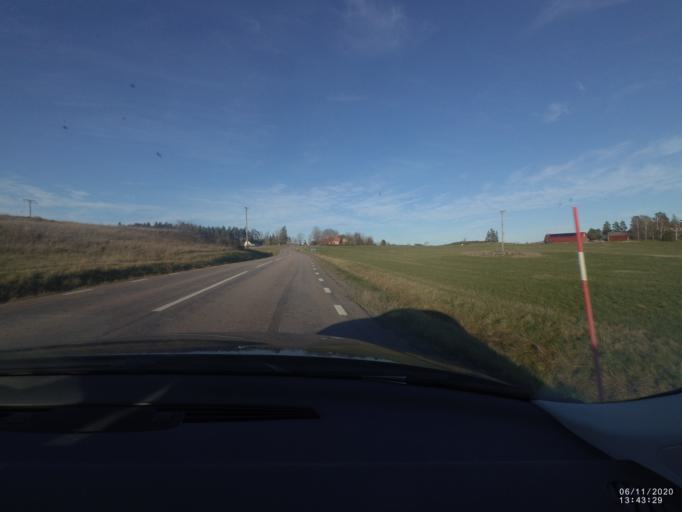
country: SE
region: Soedermanland
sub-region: Nykopings Kommun
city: Nykoping
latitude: 58.8633
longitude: 17.0655
